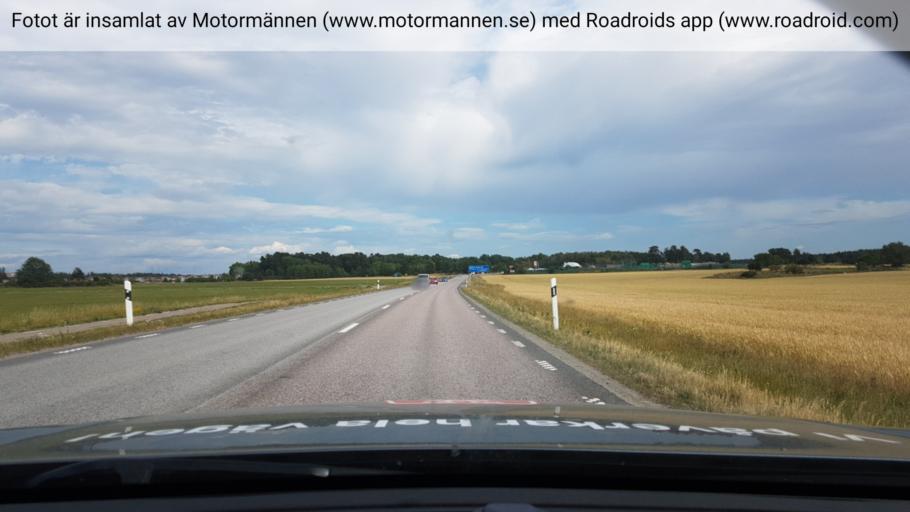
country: SE
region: Uppsala
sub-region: Uppsala Kommun
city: Uppsala
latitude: 59.8485
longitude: 17.5384
